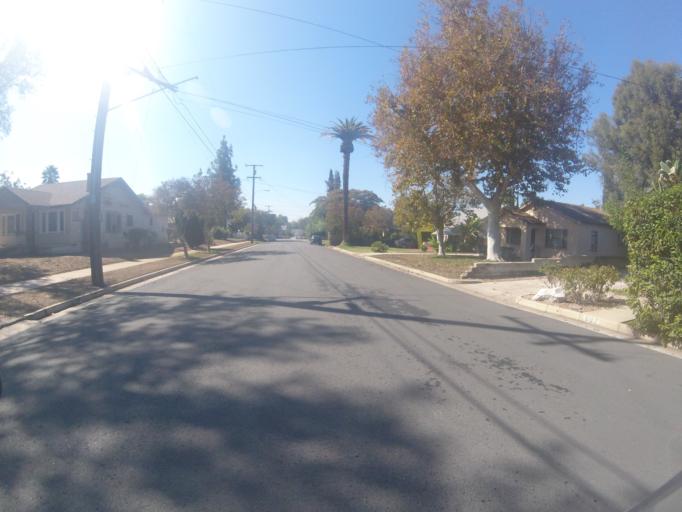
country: US
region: California
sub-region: San Bernardino County
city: Redlands
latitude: 34.0516
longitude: -117.1885
